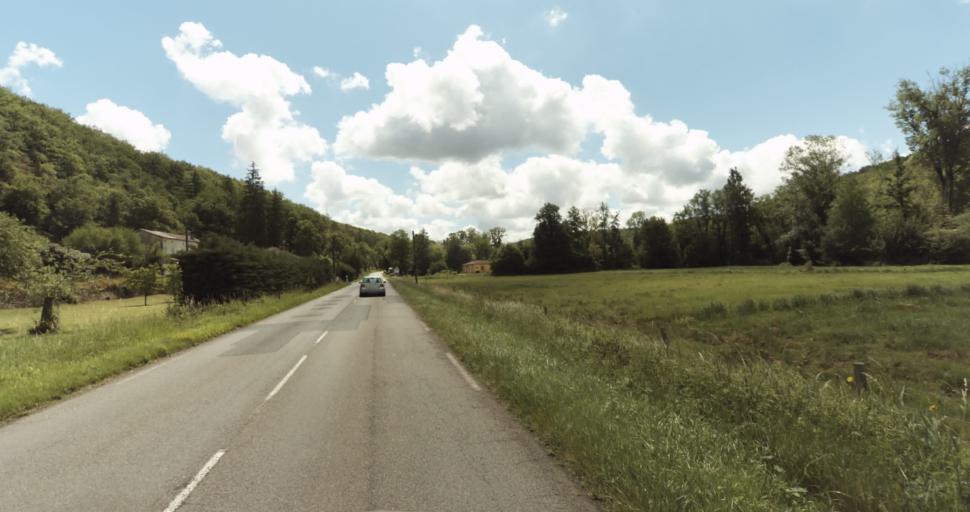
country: FR
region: Aquitaine
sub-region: Departement de la Dordogne
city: Lalinde
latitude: 44.8032
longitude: 0.7336
